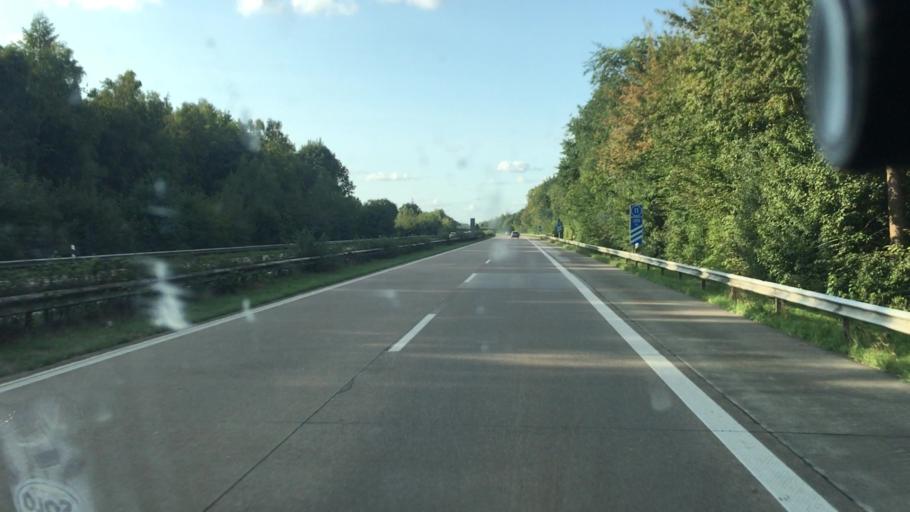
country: DE
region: Lower Saxony
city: Rastede
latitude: 53.2735
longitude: 8.1593
